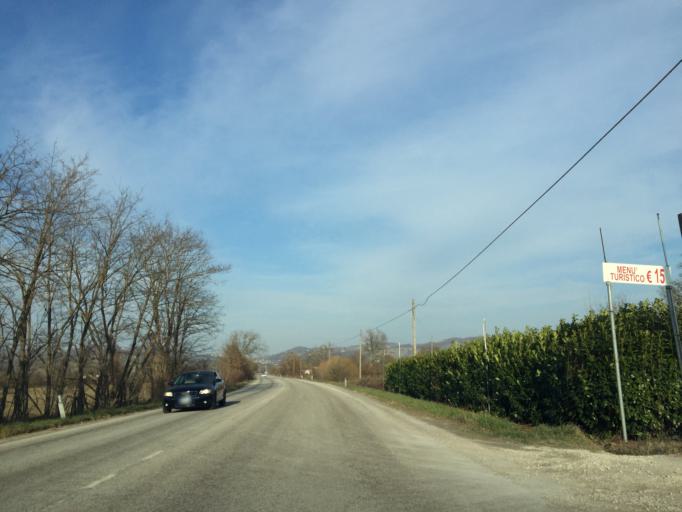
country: IT
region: Molise
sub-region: Provincia di Campobasso
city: San Massimo
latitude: 41.5056
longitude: 14.4276
